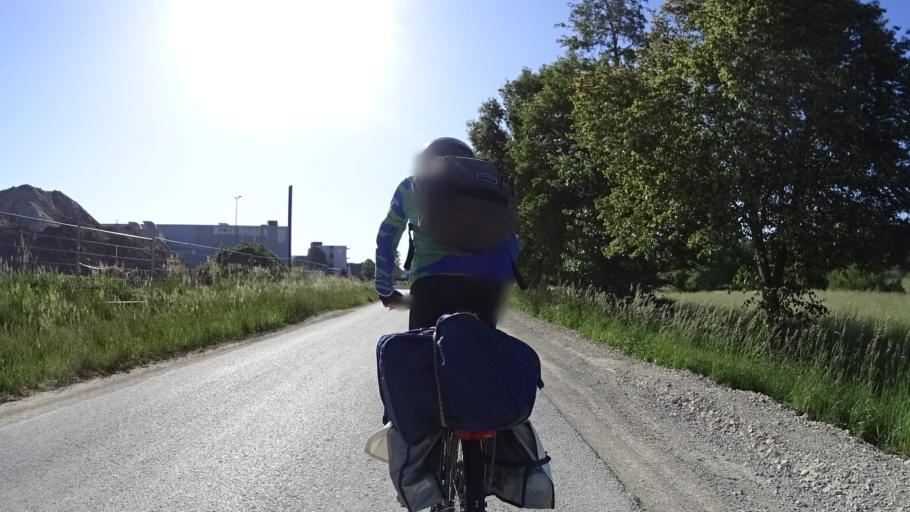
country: DE
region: Bavaria
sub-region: Regierungsbezirk Mittelfranken
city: Wieseth
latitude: 49.1584
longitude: 10.5299
